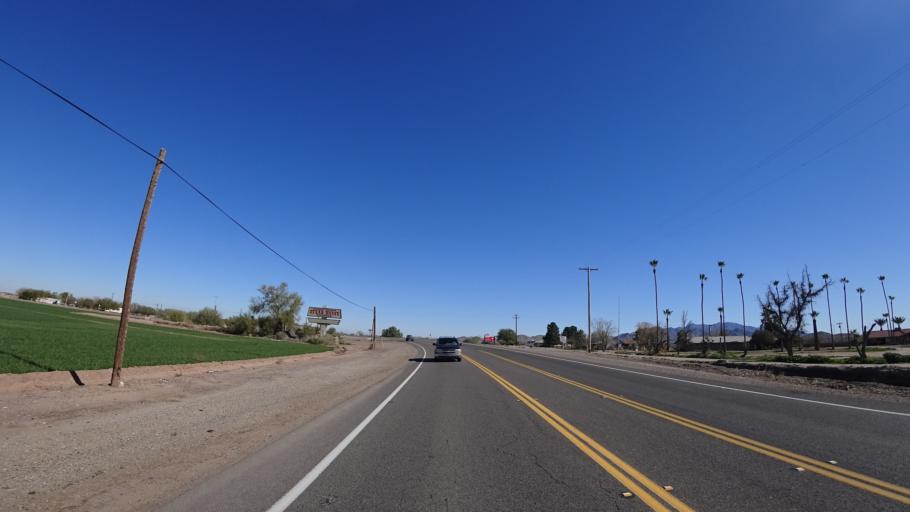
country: US
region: Arizona
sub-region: Maricopa County
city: Goodyear
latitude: 33.3774
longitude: -112.4622
